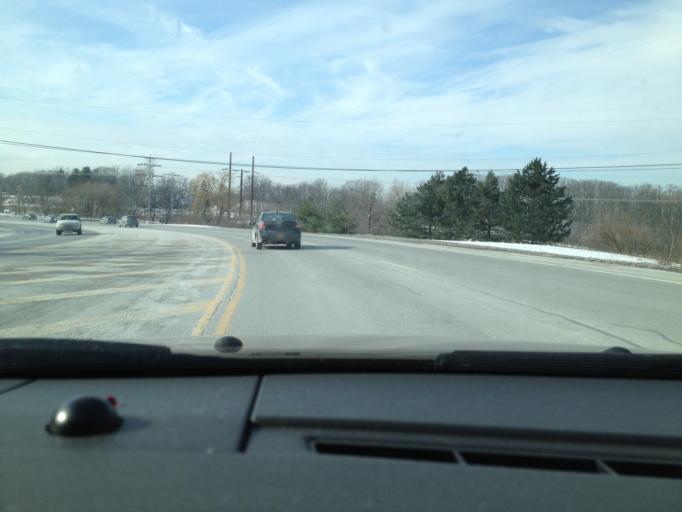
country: US
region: New York
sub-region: Albany County
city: Menands
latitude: 42.6557
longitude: -73.6971
